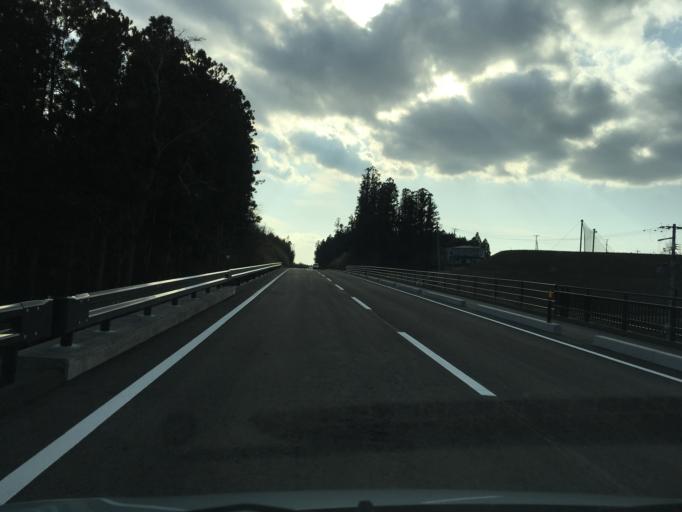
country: JP
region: Miyagi
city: Wakuya
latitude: 38.7270
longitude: 141.2827
